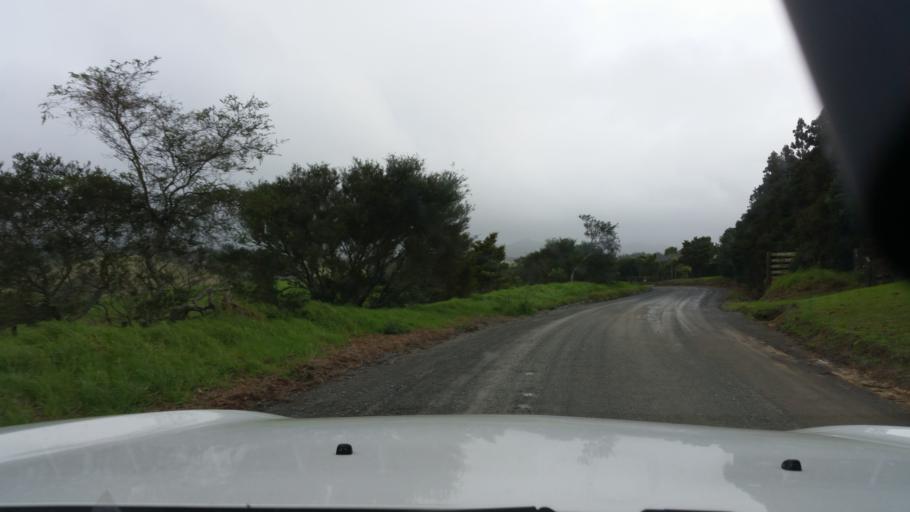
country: NZ
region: Northland
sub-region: Whangarei
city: Ngunguru
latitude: -35.7501
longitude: 174.5104
